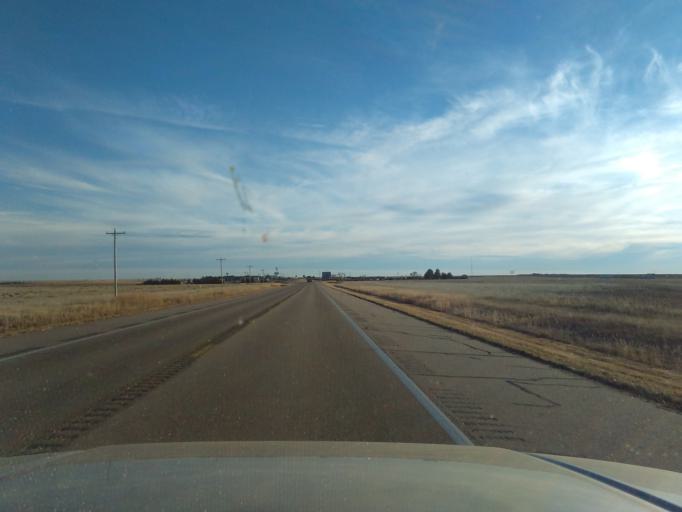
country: US
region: Kansas
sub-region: Logan County
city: Oakley
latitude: 39.1984
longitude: -100.8701
